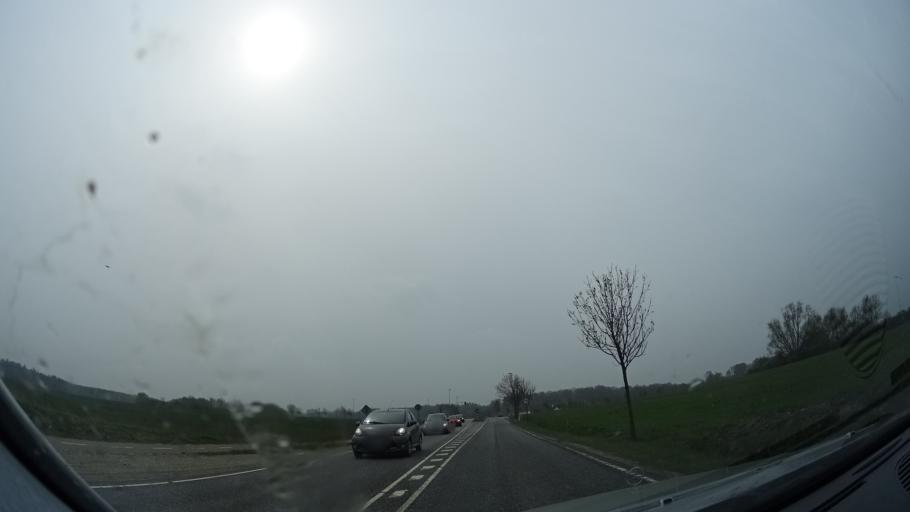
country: DK
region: Zealand
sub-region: Lejre Kommune
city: Ejby
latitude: 55.6733
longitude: 11.8316
